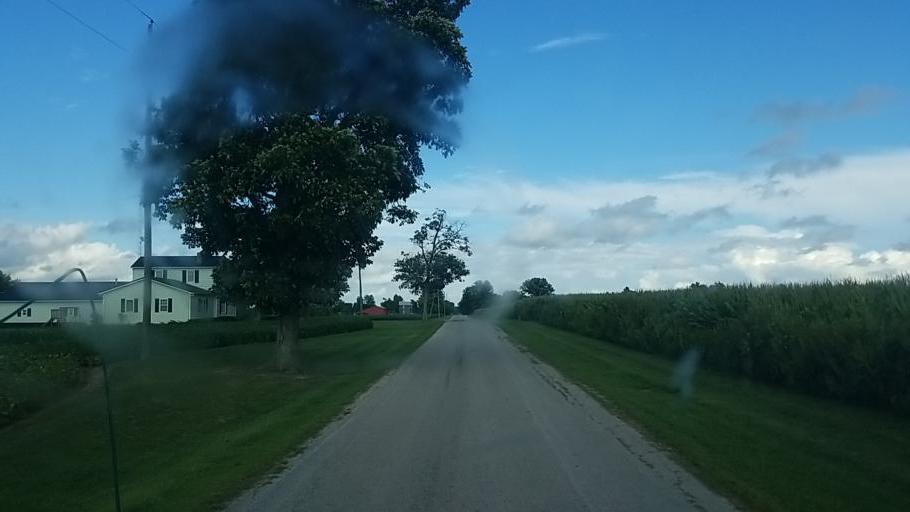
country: US
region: Ohio
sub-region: Hardin County
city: Forest
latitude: 40.7889
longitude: -83.4478
